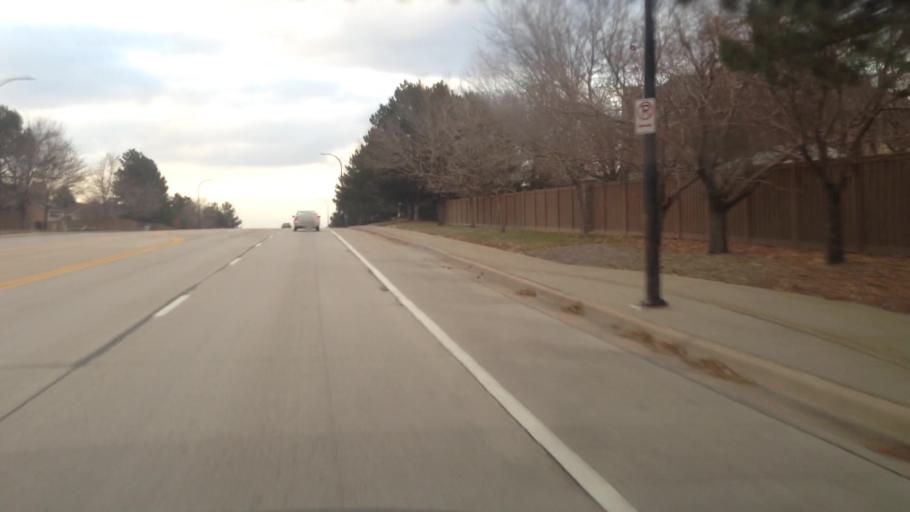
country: US
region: Colorado
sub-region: Douglas County
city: Carriage Club
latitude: 39.5375
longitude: -104.9076
